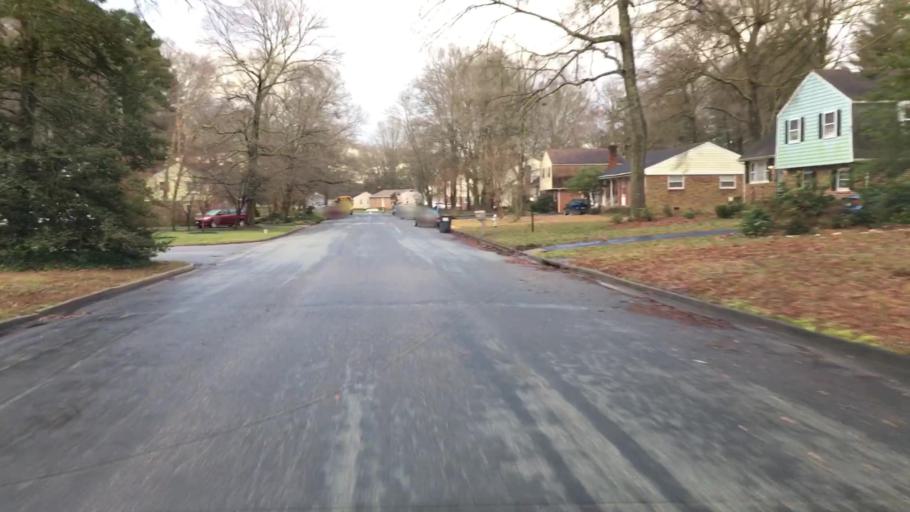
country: US
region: Virginia
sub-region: Chesterfield County
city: Bon Air
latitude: 37.5142
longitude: -77.6241
